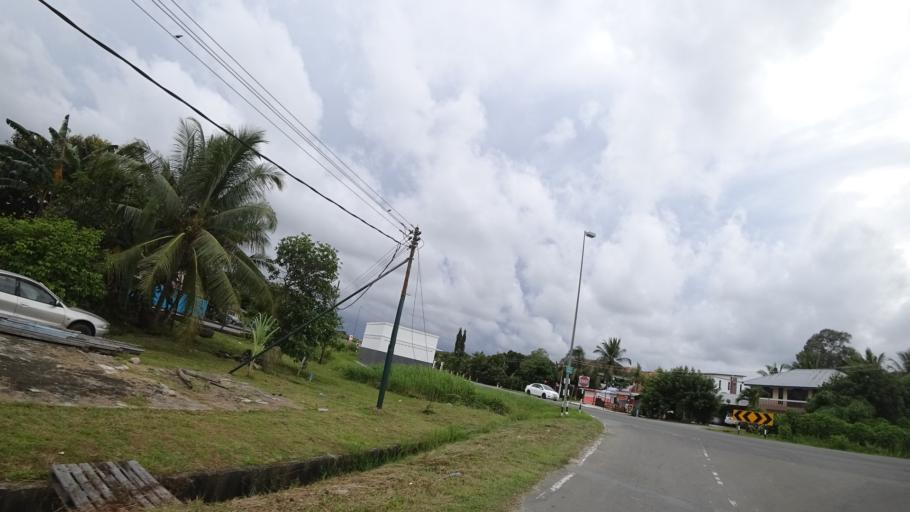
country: BN
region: Brunei and Muara
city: Bandar Seri Begawan
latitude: 4.8519
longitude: 114.8445
